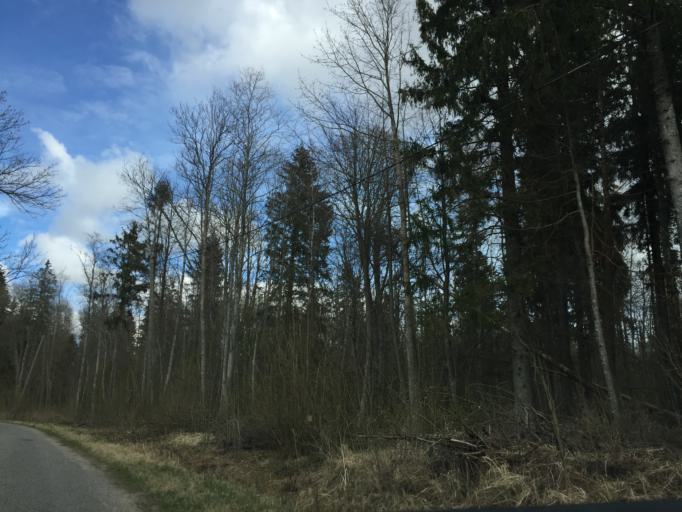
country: LV
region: Limbazu Rajons
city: Limbazi
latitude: 57.6139
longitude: 24.6859
